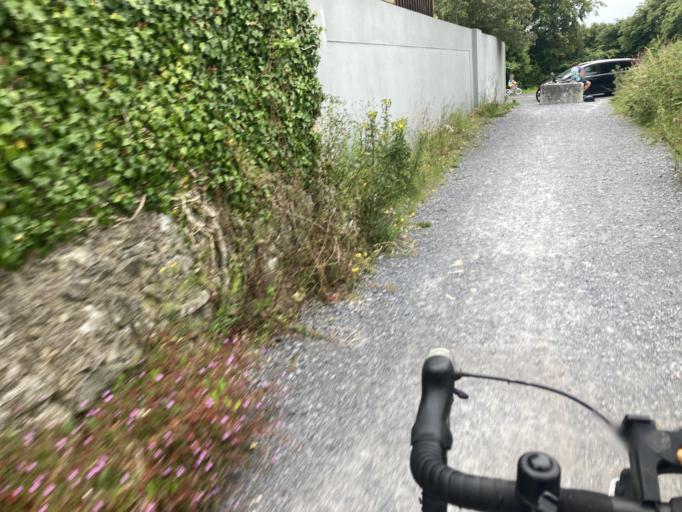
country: IE
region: Connaught
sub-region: County Galway
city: Gaillimh
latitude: 53.2682
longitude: -9.0943
